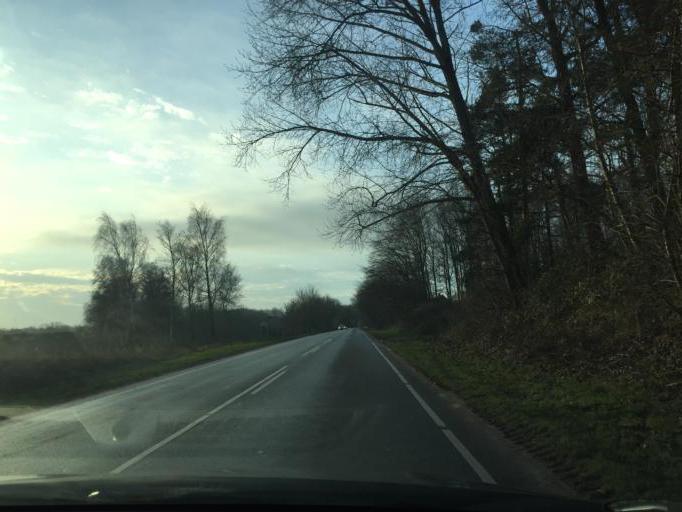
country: DK
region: South Denmark
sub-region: Faaborg-Midtfyn Kommune
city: Faaborg
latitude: 55.1655
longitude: 10.2769
